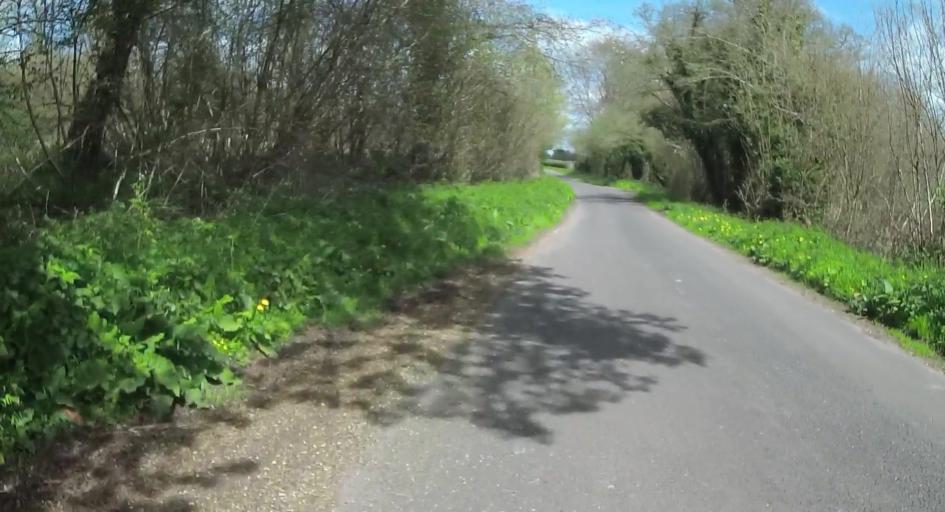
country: GB
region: England
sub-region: Hampshire
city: Romsey
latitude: 51.0713
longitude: -1.5257
